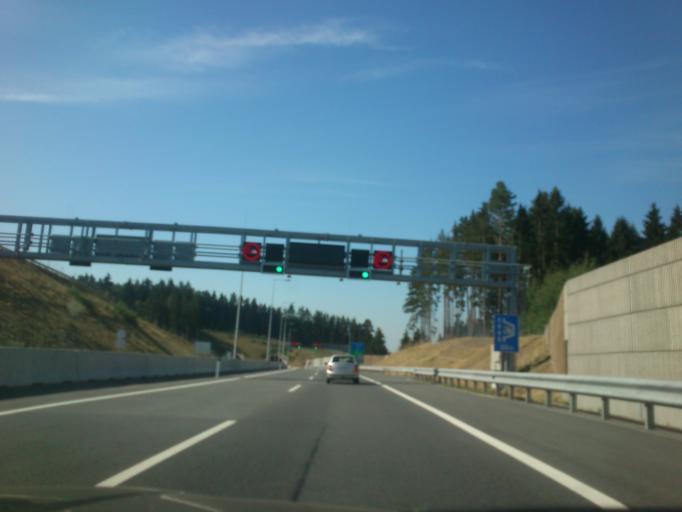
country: AT
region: Upper Austria
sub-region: Politischer Bezirk Freistadt
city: Freistadt
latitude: 48.5003
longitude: 14.5176
